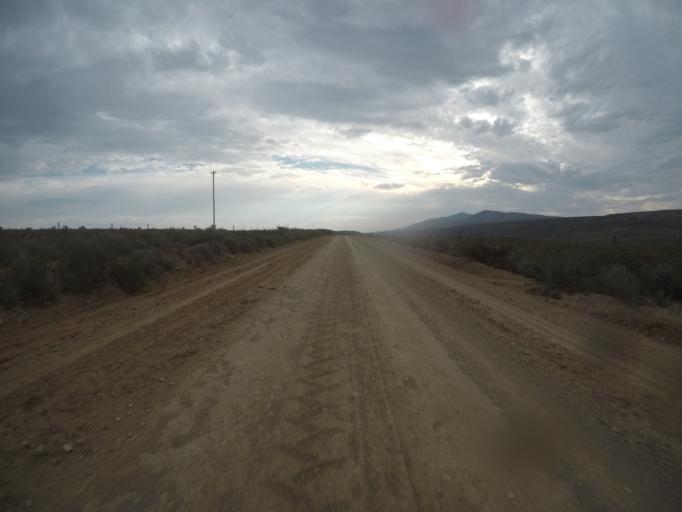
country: ZA
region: Eastern Cape
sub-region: Cacadu District Municipality
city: Willowmore
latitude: -33.4924
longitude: 23.5778
